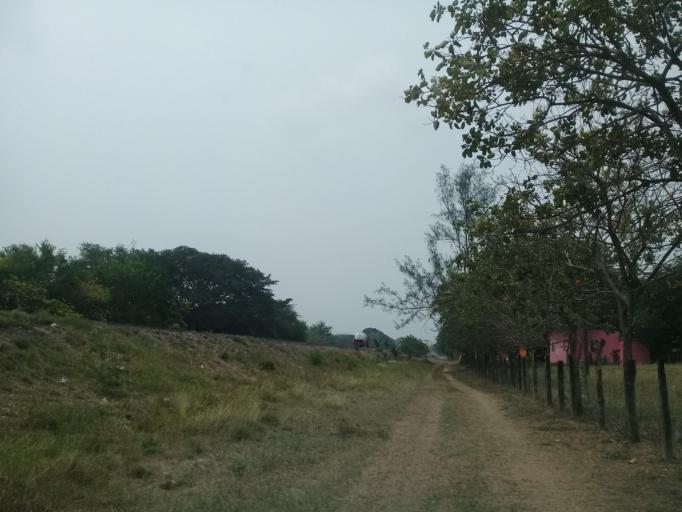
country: MX
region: Veracruz
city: Jamapa
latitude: 18.9503
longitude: -96.1977
